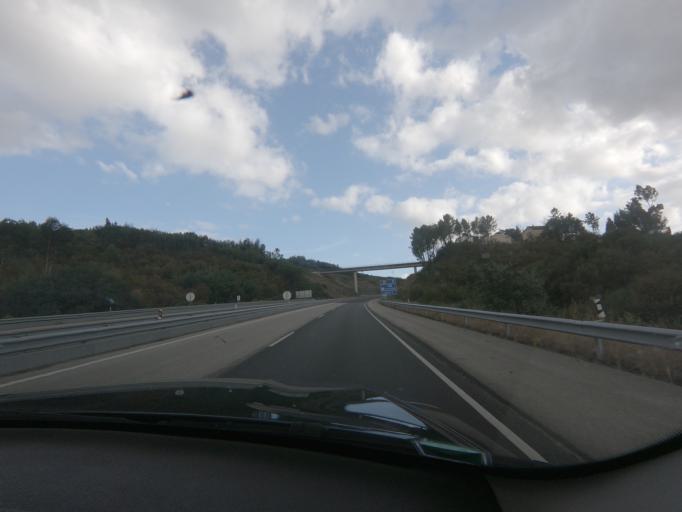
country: PT
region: Viseu
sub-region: Castro Daire
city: Castro Daire
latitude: 40.8824
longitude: -7.9201
